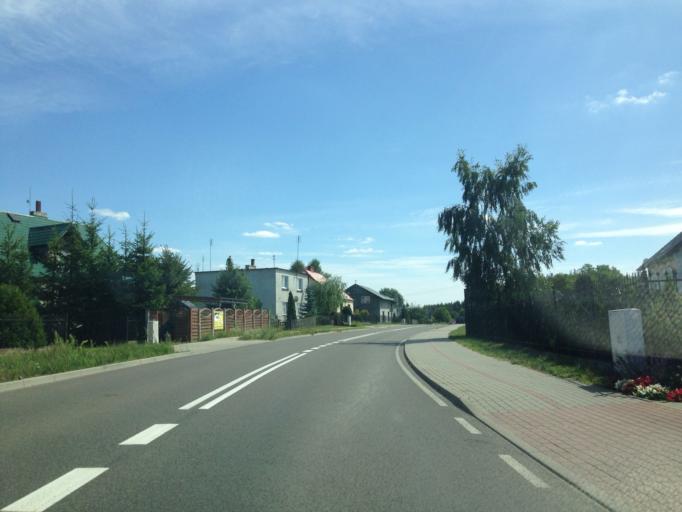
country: PL
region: Pomeranian Voivodeship
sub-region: Powiat chojnicki
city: Czersk
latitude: 53.7869
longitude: 17.9914
